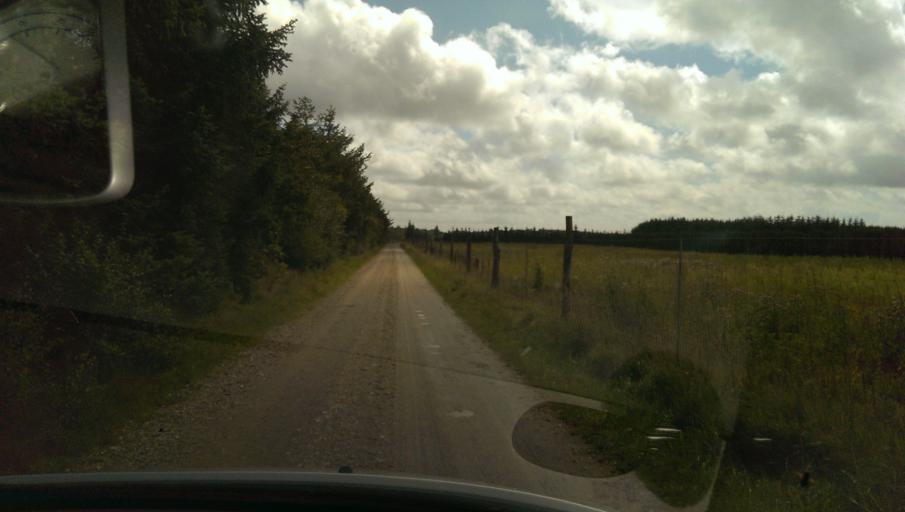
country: DK
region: South Denmark
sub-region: Varde Kommune
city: Varde
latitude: 55.6056
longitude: 8.4508
